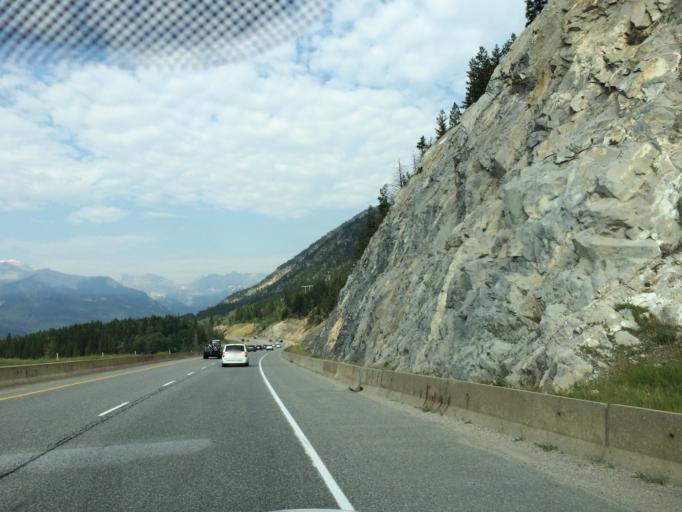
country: CA
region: Alberta
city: Banff
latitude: 51.1775
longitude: -115.6290
